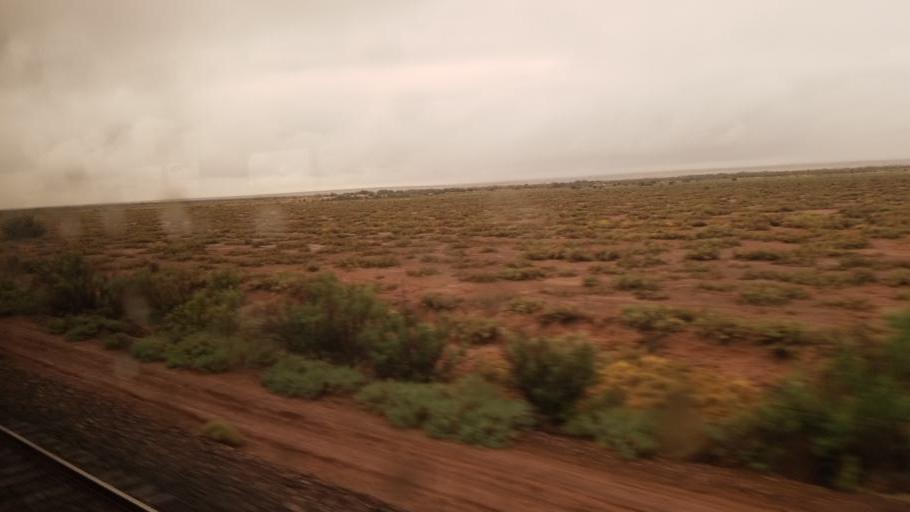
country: US
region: Arizona
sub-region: Navajo County
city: Winslow
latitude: 35.0005
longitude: -110.6315
